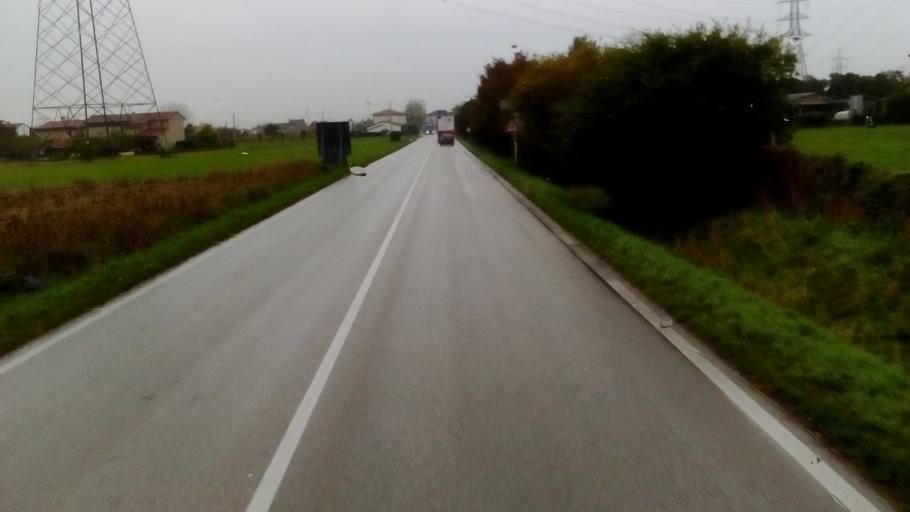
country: IT
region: Veneto
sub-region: Provincia di Vicenza
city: Montecchio Precalcino
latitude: 45.6740
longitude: 11.5725
